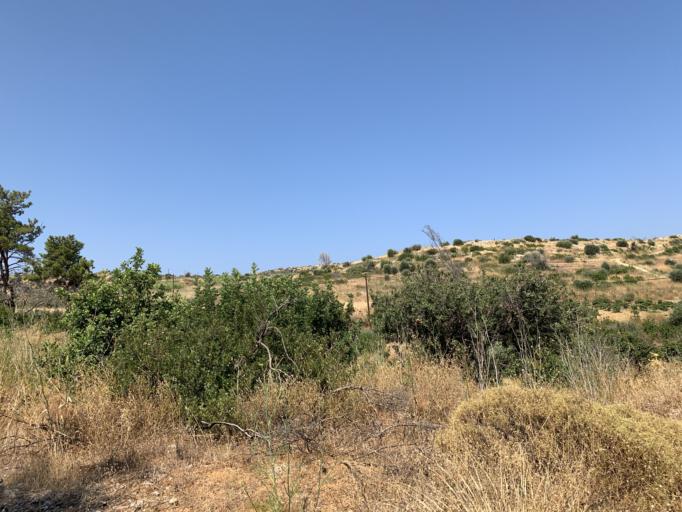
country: GR
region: North Aegean
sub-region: Chios
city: Thymiana
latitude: 38.3060
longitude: 26.0005
